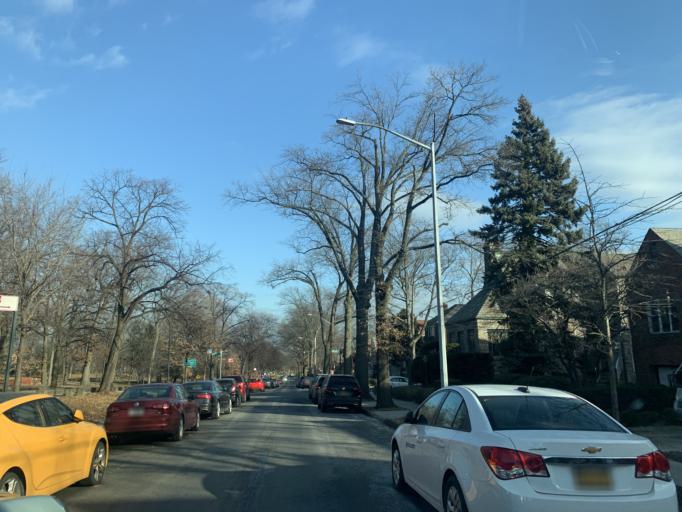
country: US
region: New York
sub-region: Bronx
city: The Bronx
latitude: 40.8571
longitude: -73.8544
